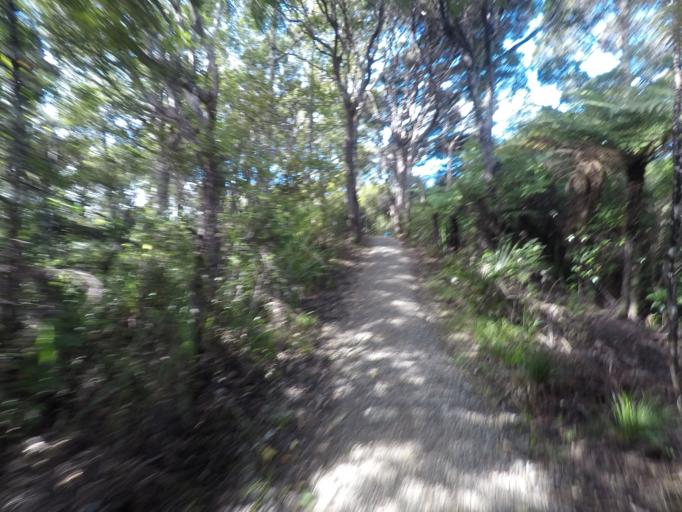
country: NZ
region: Auckland
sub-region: Auckland
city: Titirangi
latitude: -37.0318
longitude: 174.5229
